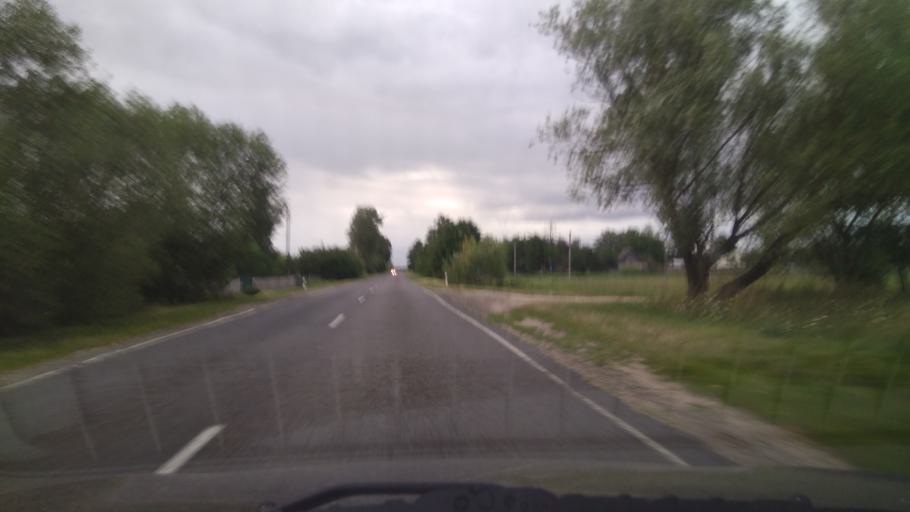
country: BY
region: Brest
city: Byaroza
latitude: 52.4241
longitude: 24.9811
